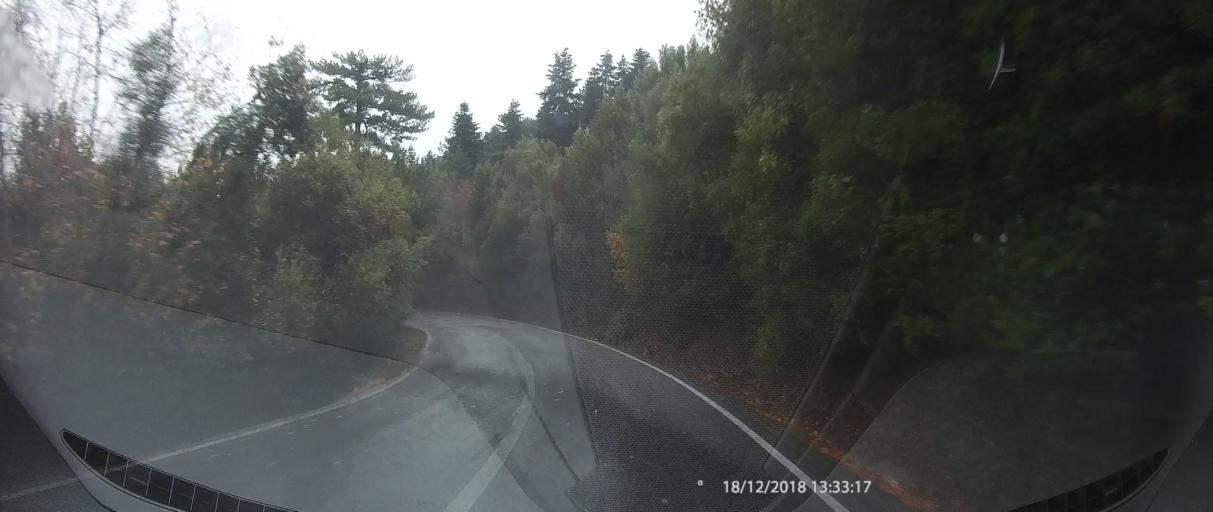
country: GR
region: Central Macedonia
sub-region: Nomos Pierias
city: Litochoro
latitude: 40.1177
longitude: 22.4794
